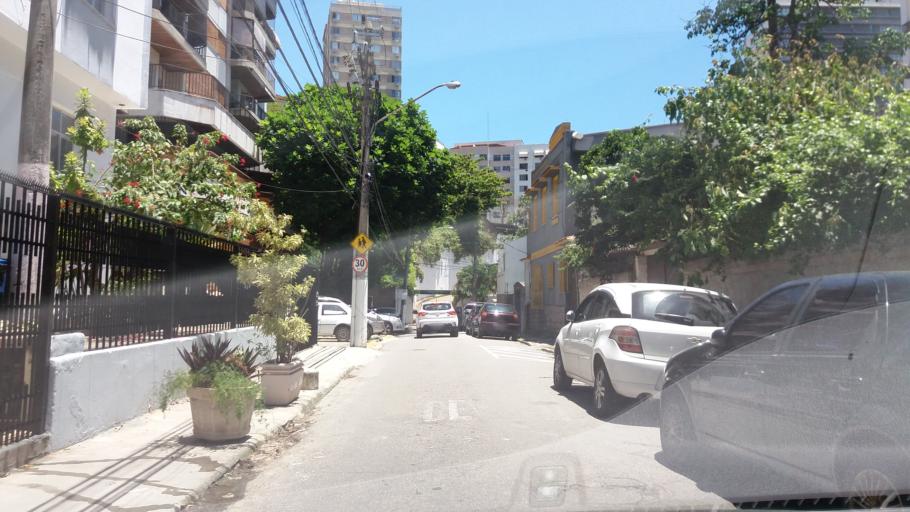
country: BR
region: Rio de Janeiro
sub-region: Niteroi
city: Niteroi
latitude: -22.9033
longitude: -43.1207
